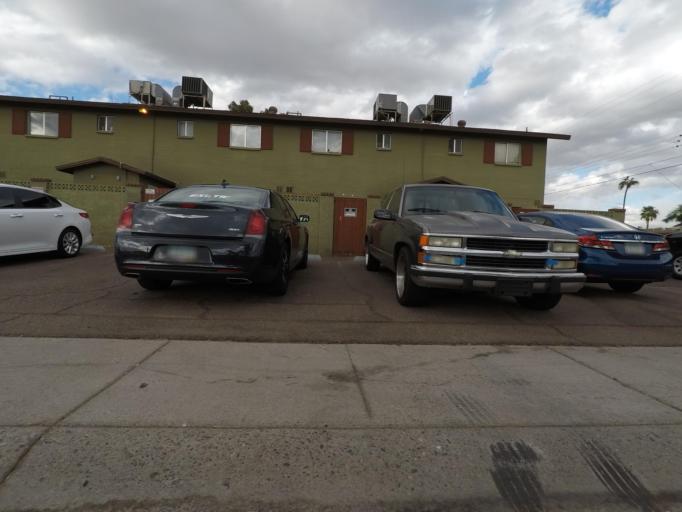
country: US
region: Arizona
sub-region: Maricopa County
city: Glendale
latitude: 33.5035
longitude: -112.1424
